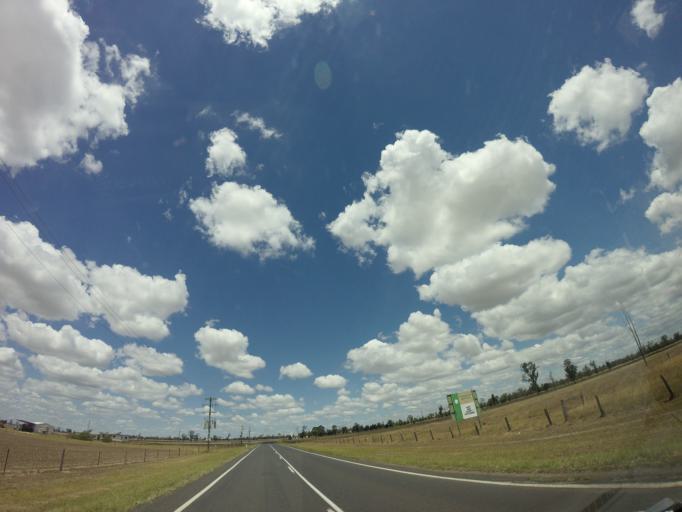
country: AU
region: Queensland
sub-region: Toowoomba
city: Oakey
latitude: -27.8734
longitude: 151.2432
